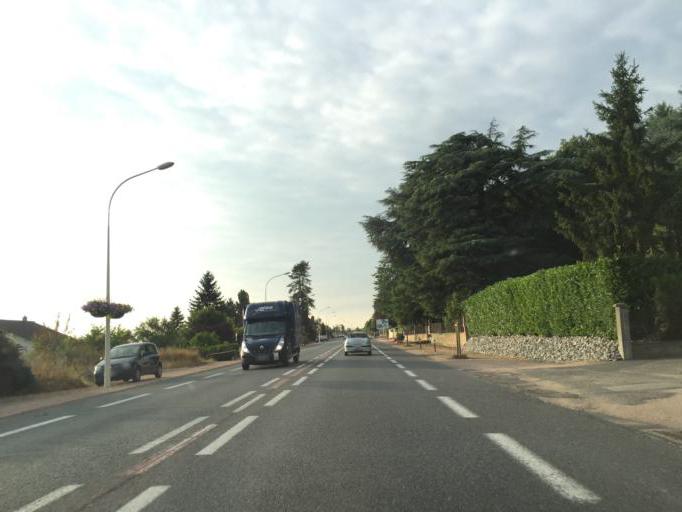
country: FR
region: Auvergne
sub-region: Departement de l'Allier
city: Varennes-sur-Allier
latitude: 46.3227
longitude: 3.3910
